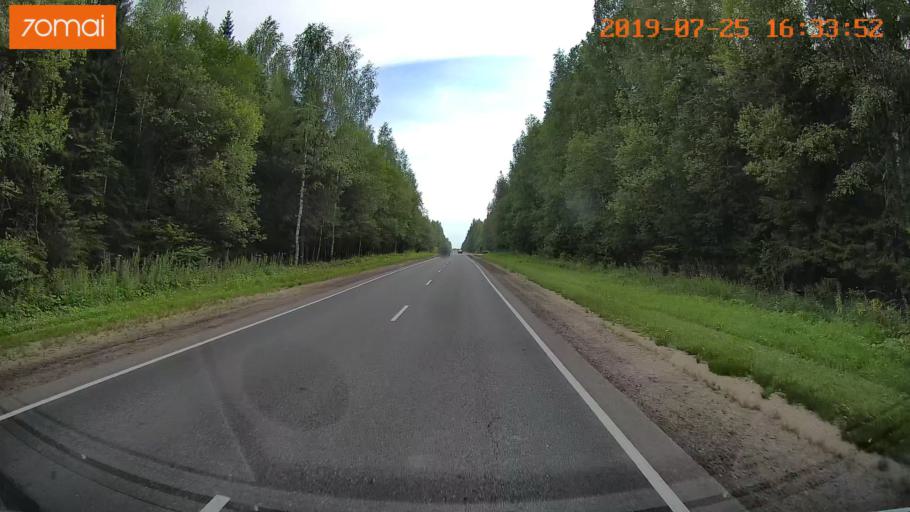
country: RU
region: Ivanovo
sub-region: Privolzhskiy Rayon
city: Ples
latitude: 57.4226
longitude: 41.4480
